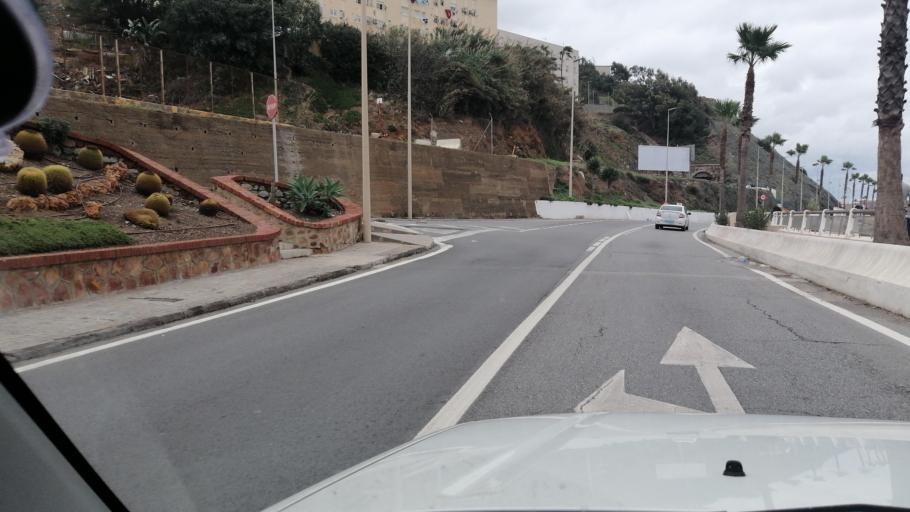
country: ES
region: Ceuta
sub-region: Ceuta
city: Ceuta
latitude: 35.8796
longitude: -5.3277
